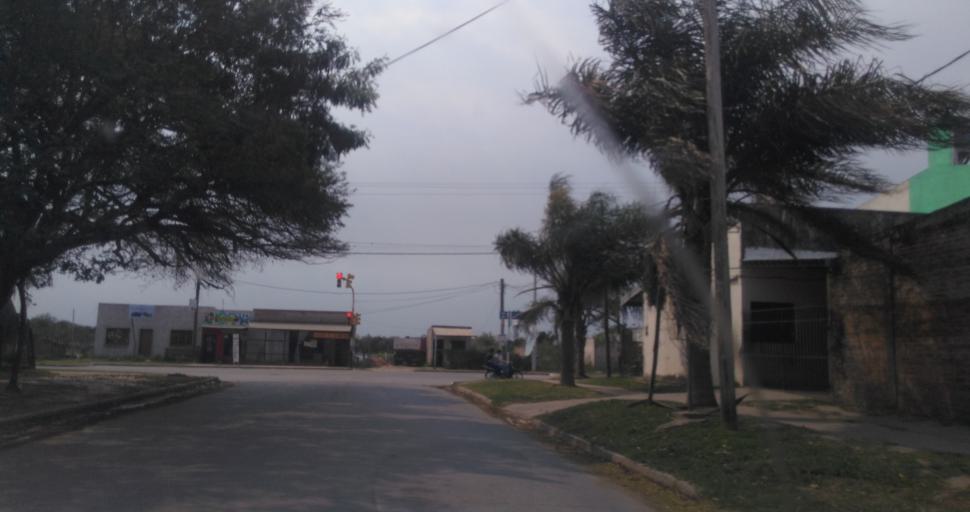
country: AR
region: Chaco
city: Fontana
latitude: -27.4177
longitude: -59.0248
